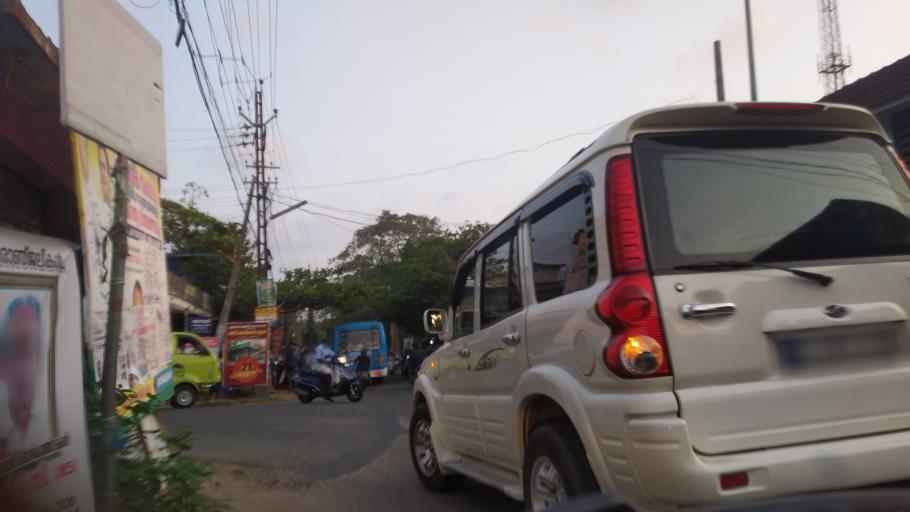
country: IN
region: Kerala
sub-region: Thrissur District
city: Kodungallur
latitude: 10.2360
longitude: 76.1531
